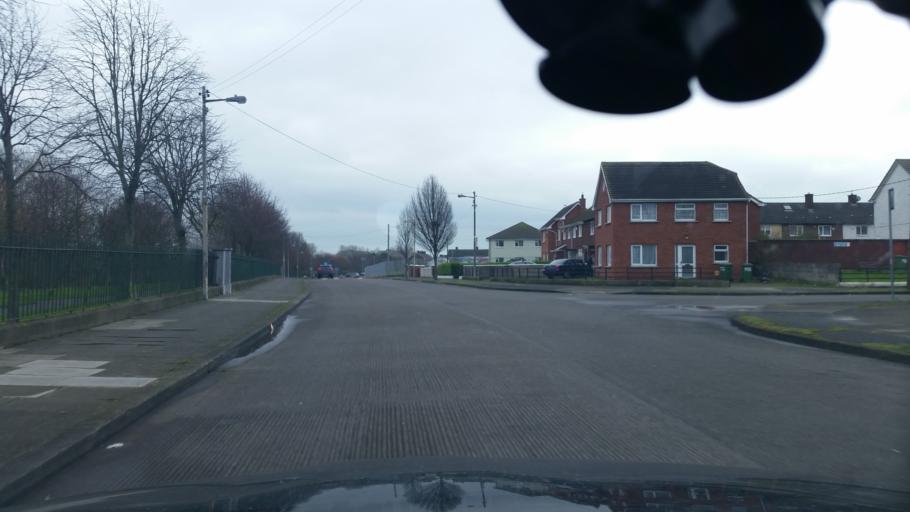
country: IE
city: Bonnybrook
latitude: 53.3962
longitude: -6.2076
